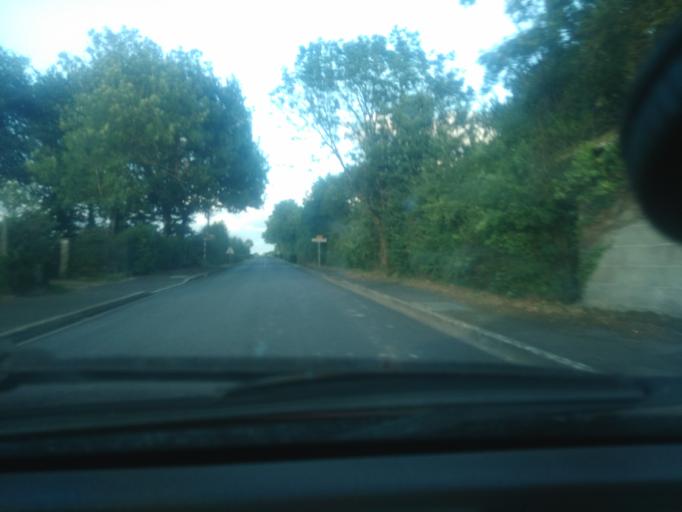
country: FR
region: Pays de la Loire
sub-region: Departement de la Vendee
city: La Ferriere
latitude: 46.7125
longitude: -1.3043
